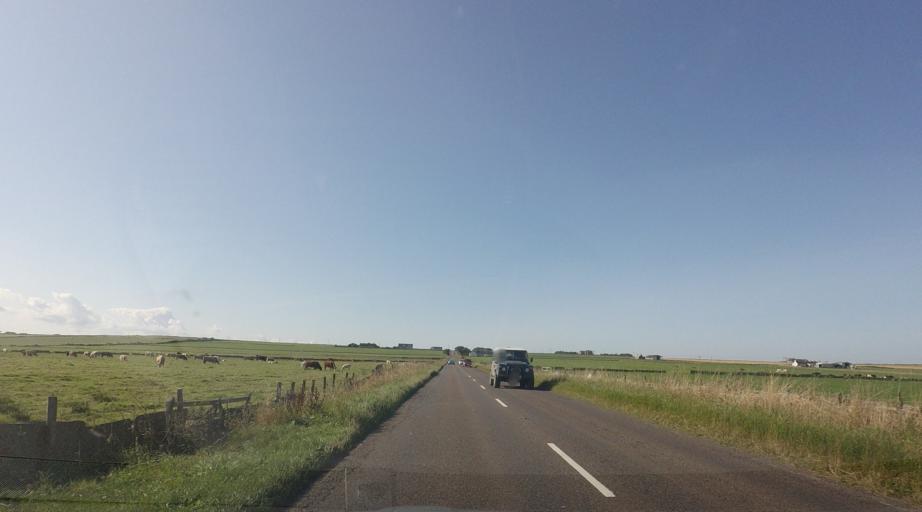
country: GB
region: Scotland
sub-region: Highland
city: Thurso
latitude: 58.5939
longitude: -3.4582
